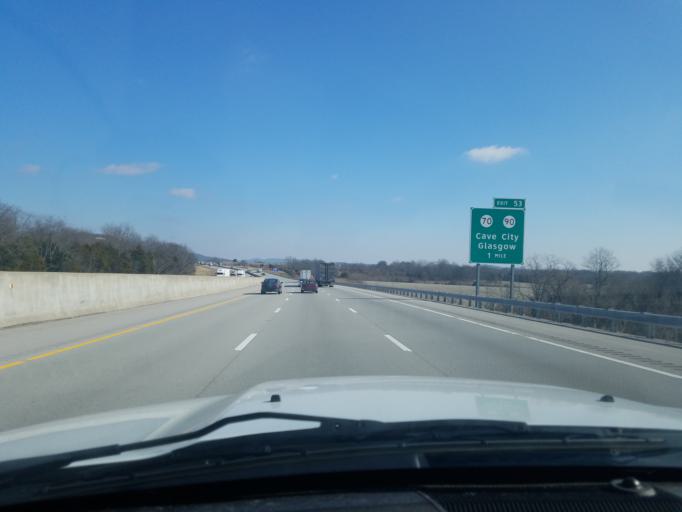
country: US
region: Kentucky
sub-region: Barren County
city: Cave City
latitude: 37.1241
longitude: -85.9929
